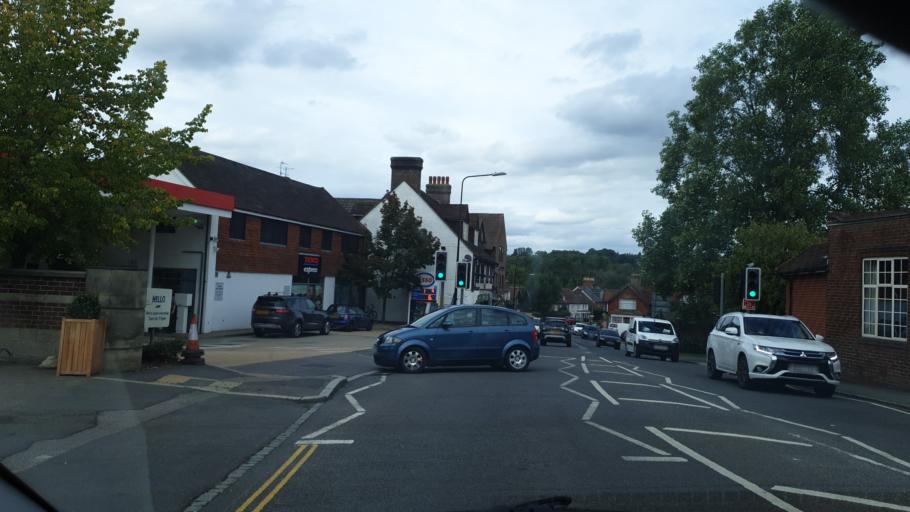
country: GB
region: England
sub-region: East Sussex
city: Forest Row
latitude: 51.0985
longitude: 0.0331
